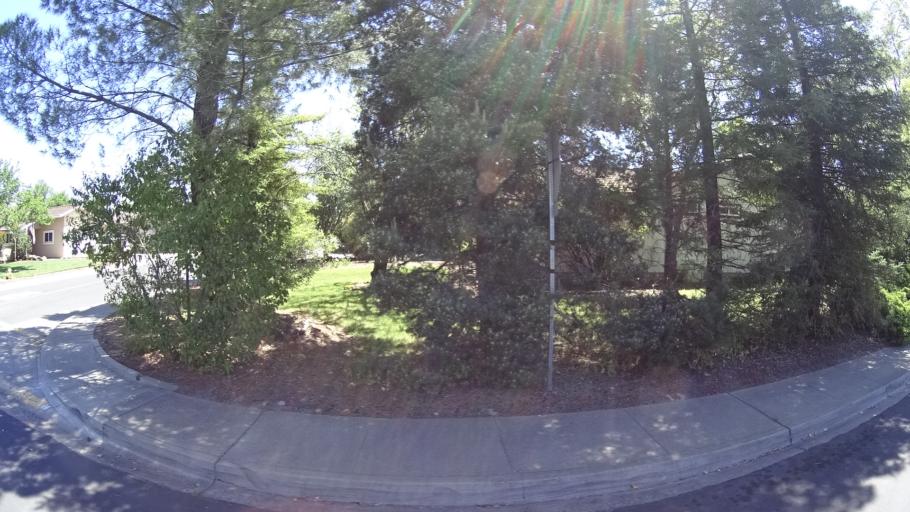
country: US
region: California
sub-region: Placer County
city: Rocklin
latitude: 38.7944
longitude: -121.2552
